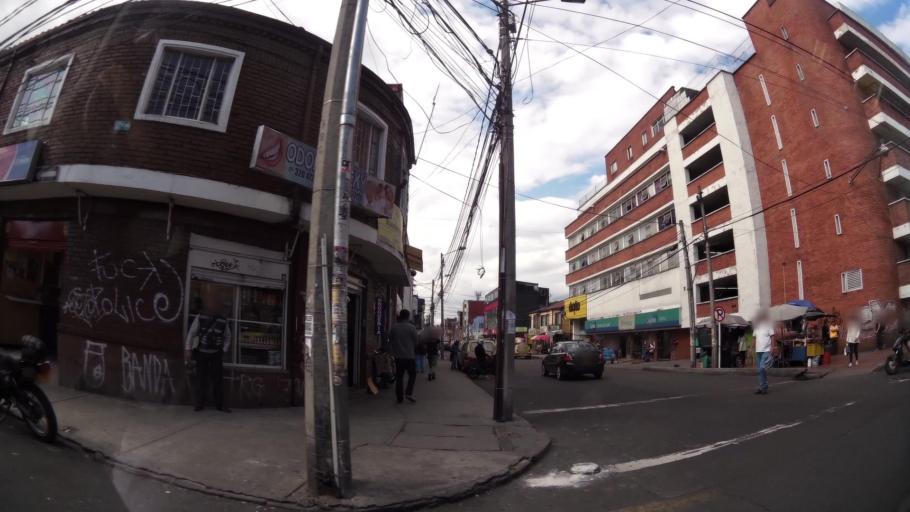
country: CO
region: Bogota D.C.
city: Bogota
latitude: 4.6388
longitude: -74.0687
